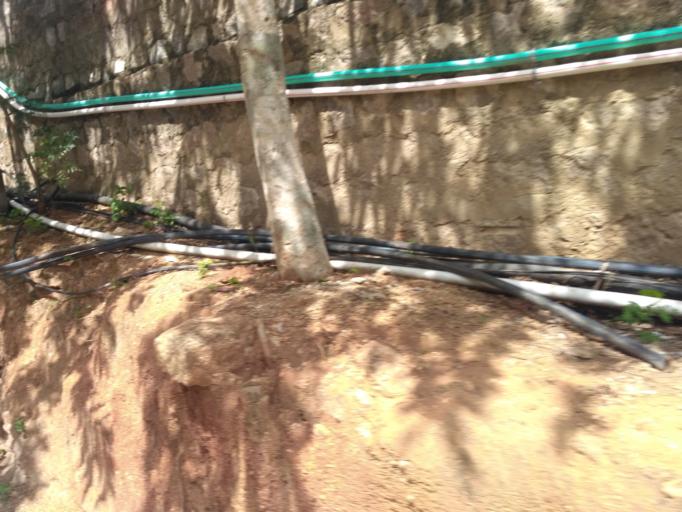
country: IN
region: Telangana
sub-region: Rangareddi
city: Kukatpalli
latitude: 17.4361
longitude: 78.3601
